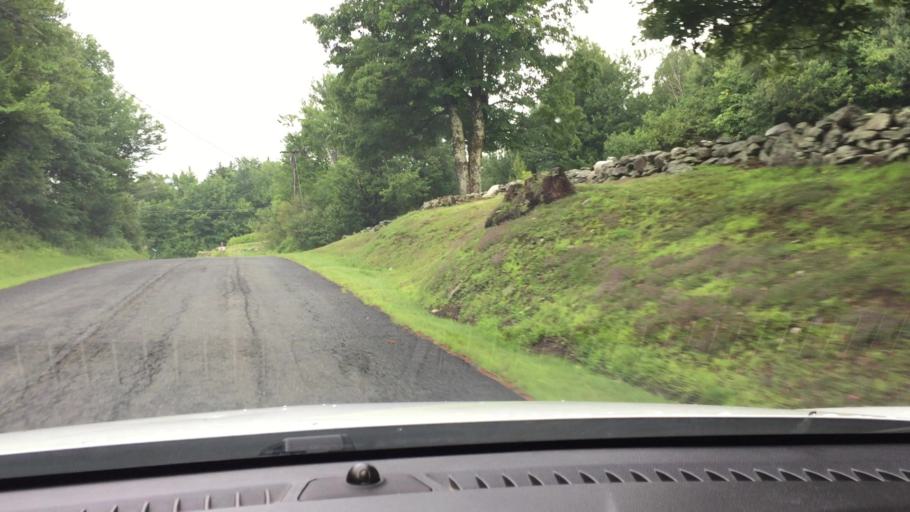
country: US
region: Massachusetts
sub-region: Berkshire County
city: Hinsdale
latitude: 42.4358
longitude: -73.0487
